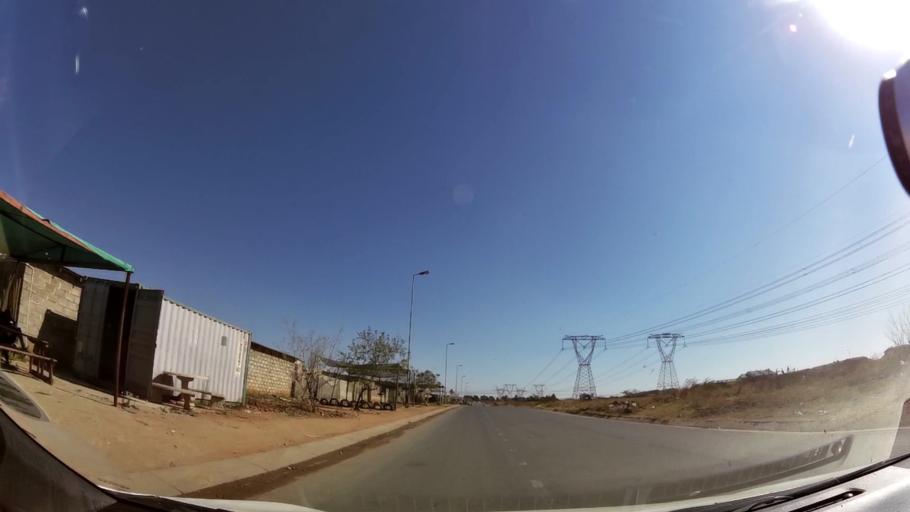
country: ZA
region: Gauteng
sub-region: City of Johannesburg Metropolitan Municipality
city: Diepsloot
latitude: -25.9050
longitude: 28.0933
